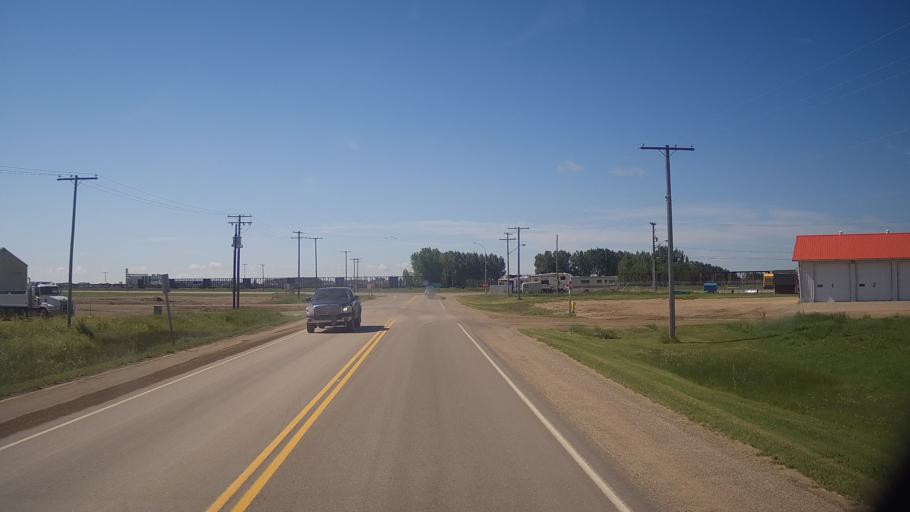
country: CA
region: Saskatchewan
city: Watrous
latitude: 51.6676
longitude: -105.4516
